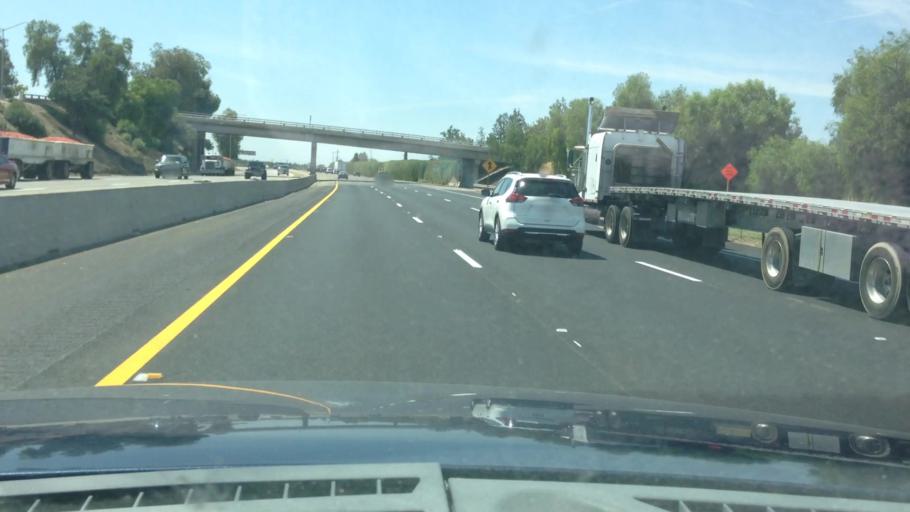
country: US
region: California
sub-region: Kern County
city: McFarland
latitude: 35.6745
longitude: -119.2268
